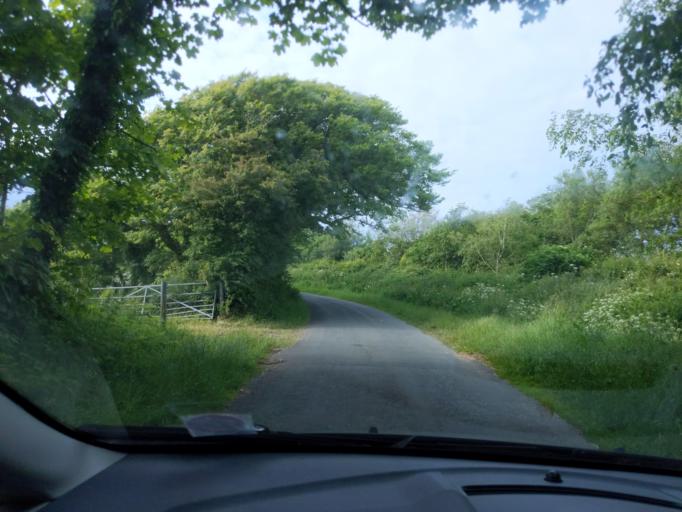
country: IM
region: Ramsey
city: Ramsey
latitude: 54.3600
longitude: -4.4408
